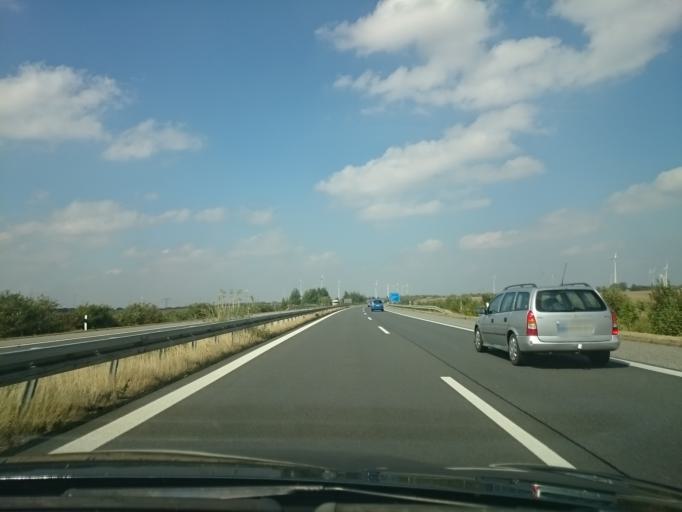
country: DE
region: Brandenburg
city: Schenkenberg
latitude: 53.3464
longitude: 13.9760
